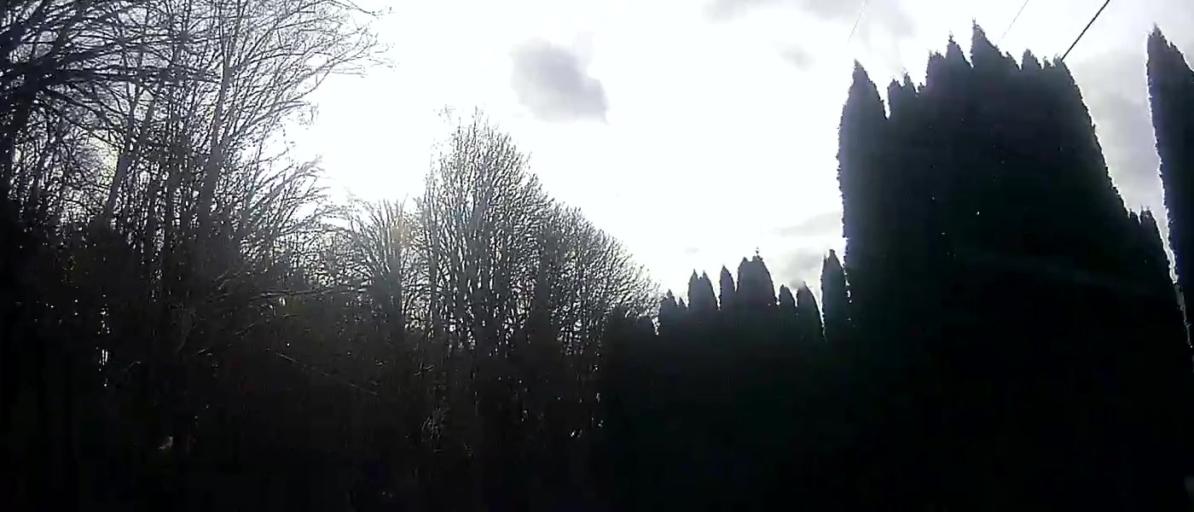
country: US
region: Washington
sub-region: Skagit County
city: Sedro-Woolley
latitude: 48.5719
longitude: -122.2981
